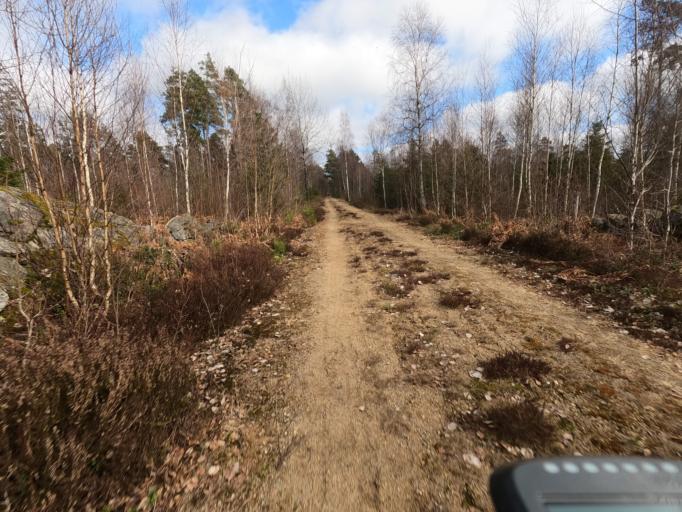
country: SE
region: Kronoberg
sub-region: Alvesta Kommun
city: Vislanda
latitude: 56.8226
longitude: 14.3093
